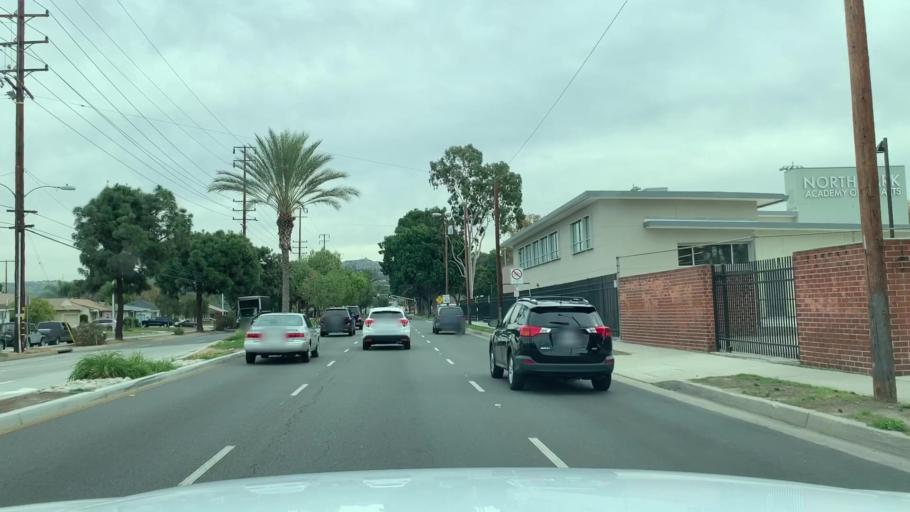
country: US
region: California
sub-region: Los Angeles County
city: Montebello
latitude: 34.0089
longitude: -118.0759
